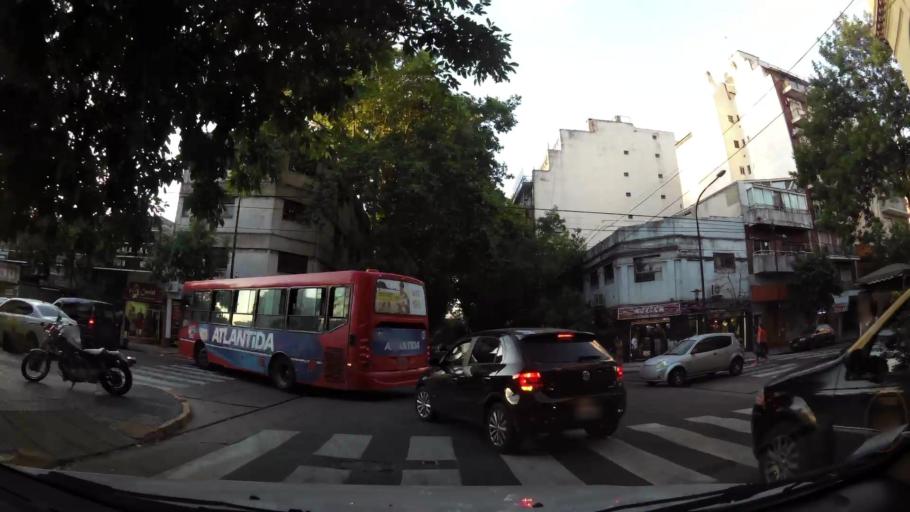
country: AR
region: Buenos Aires F.D.
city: Colegiales
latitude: -34.6016
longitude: -58.4428
